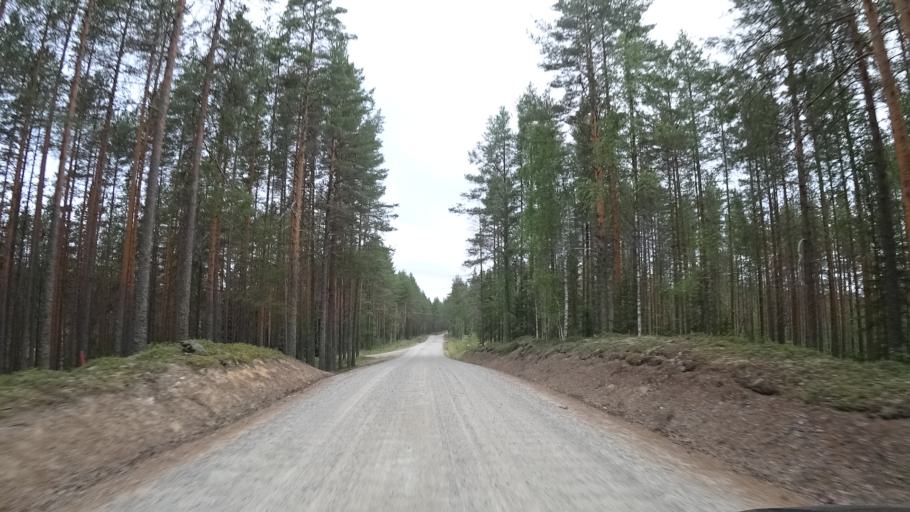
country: FI
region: North Karelia
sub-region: Pielisen Karjala
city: Lieksa
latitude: 63.2458
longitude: 30.3407
